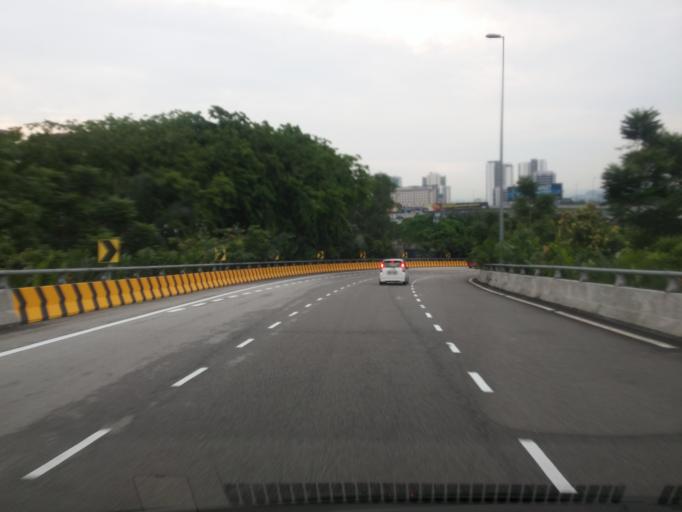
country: MY
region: Kuala Lumpur
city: Kuala Lumpur
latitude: 3.1359
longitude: 101.7193
